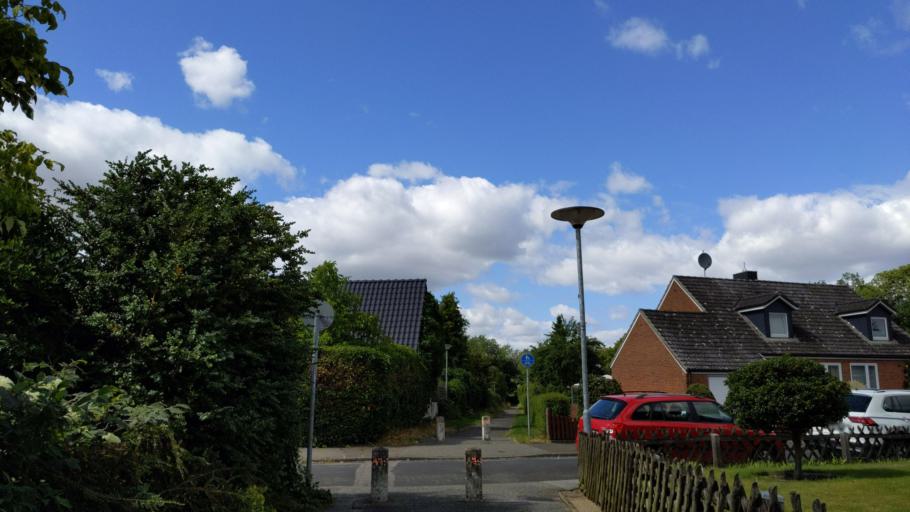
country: DE
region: Schleswig-Holstein
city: Bad Schwartau
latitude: 53.8936
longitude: 10.7149
